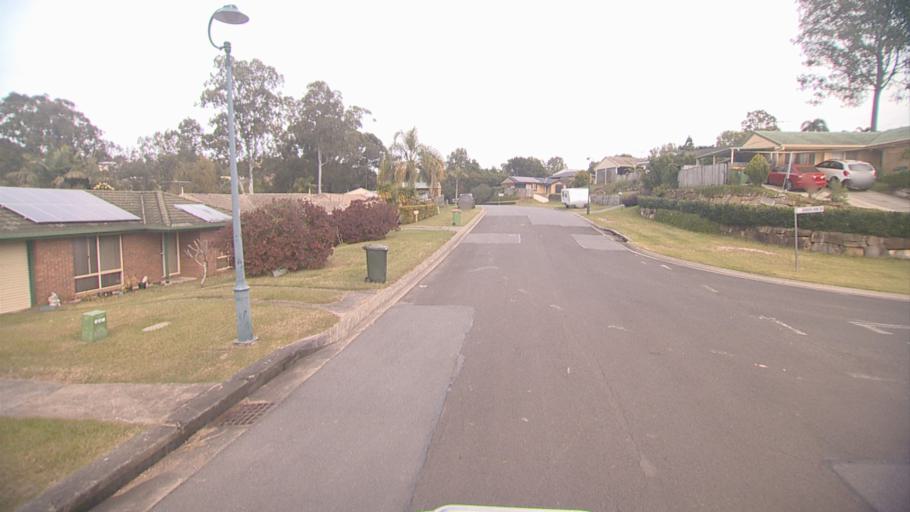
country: AU
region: Queensland
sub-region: Logan
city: Beenleigh
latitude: -27.7033
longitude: 153.1773
